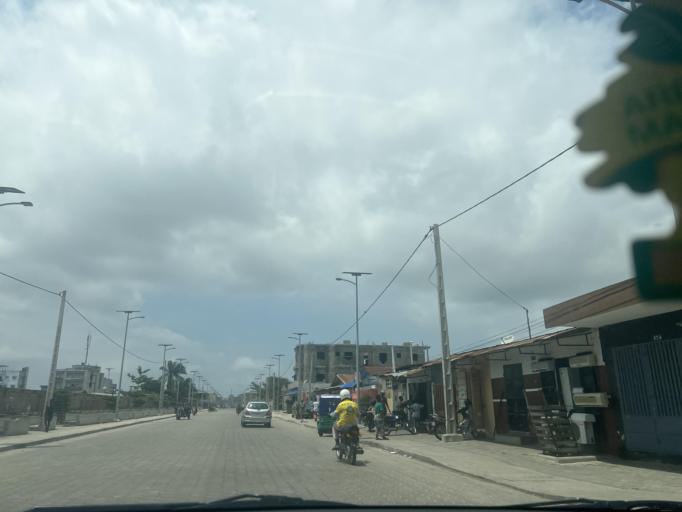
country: BJ
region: Littoral
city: Cotonou
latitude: 6.3840
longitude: 2.4509
